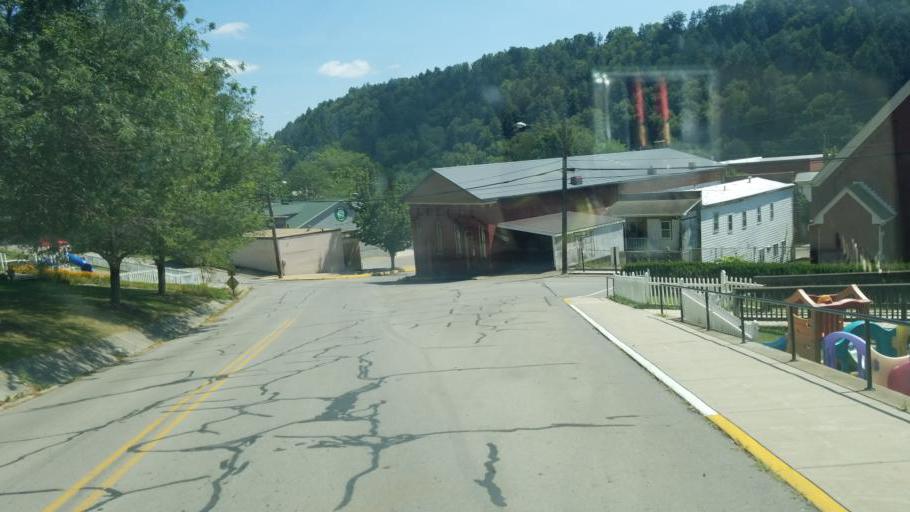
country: US
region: Pennsylvania
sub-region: Clarion County
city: Knox
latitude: 41.1779
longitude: -79.7089
